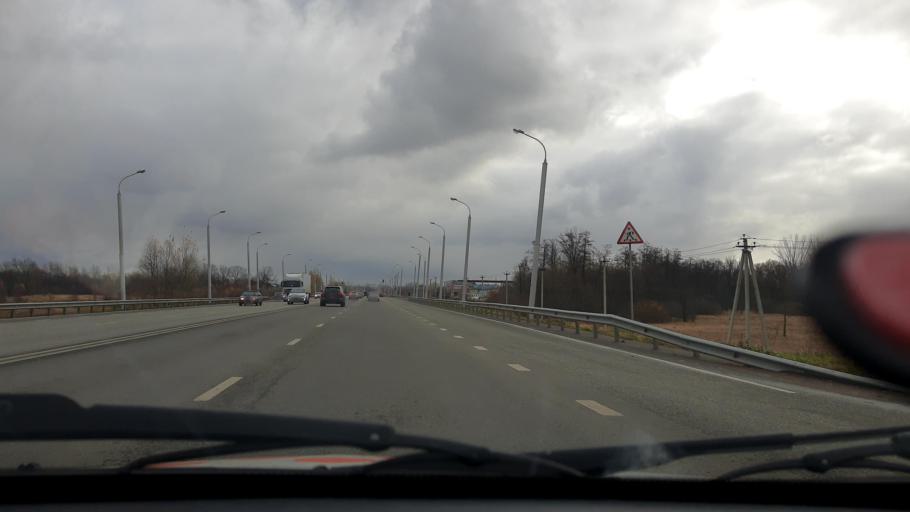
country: RU
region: Bashkortostan
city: Ufa
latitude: 54.8059
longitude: 56.1789
